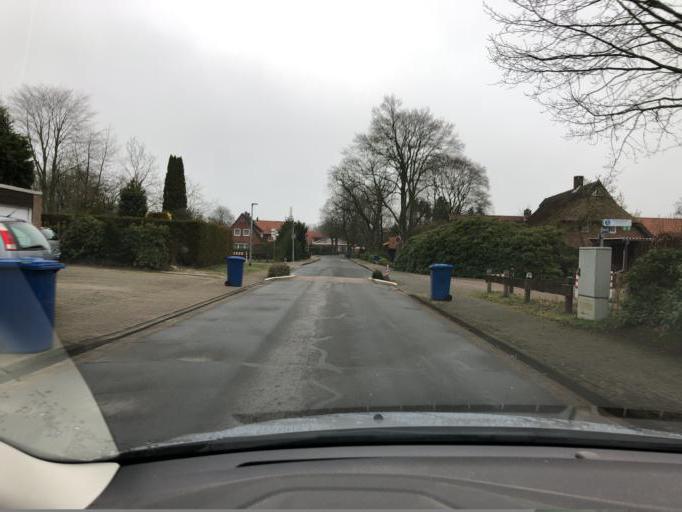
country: DE
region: Lower Saxony
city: Bad Zwischenahn
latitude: 53.1787
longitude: 8.0131
